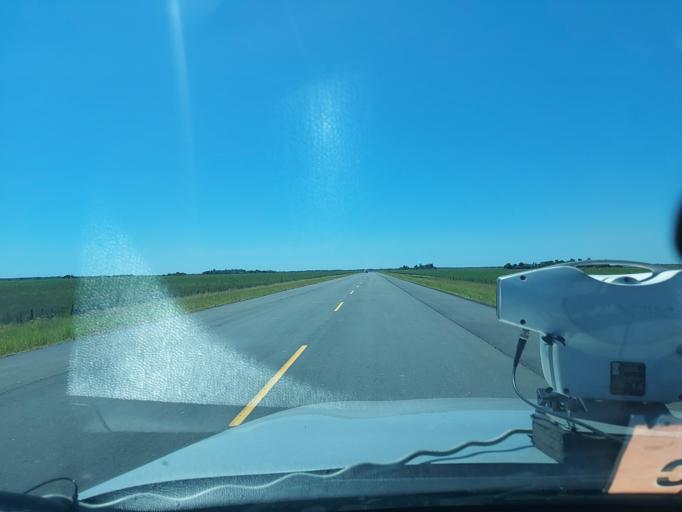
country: PY
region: Neembucu
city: Pilar
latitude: -26.8282
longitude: -58.2391
